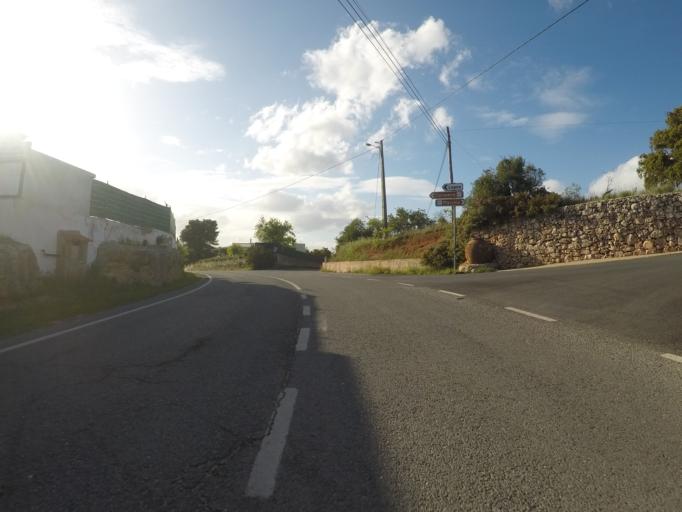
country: PT
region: Faro
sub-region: Lagoa
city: Carvoeiro
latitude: 37.1107
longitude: -8.4460
